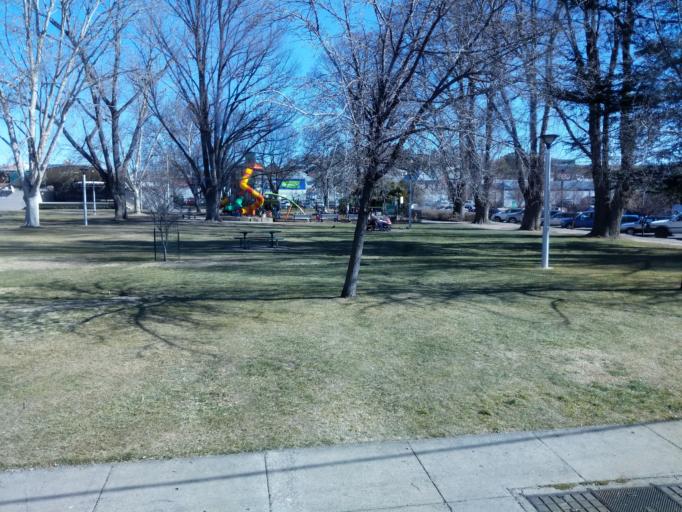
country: AU
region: New South Wales
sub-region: Cooma-Monaro
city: Cooma
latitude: -36.2339
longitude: 149.1263
